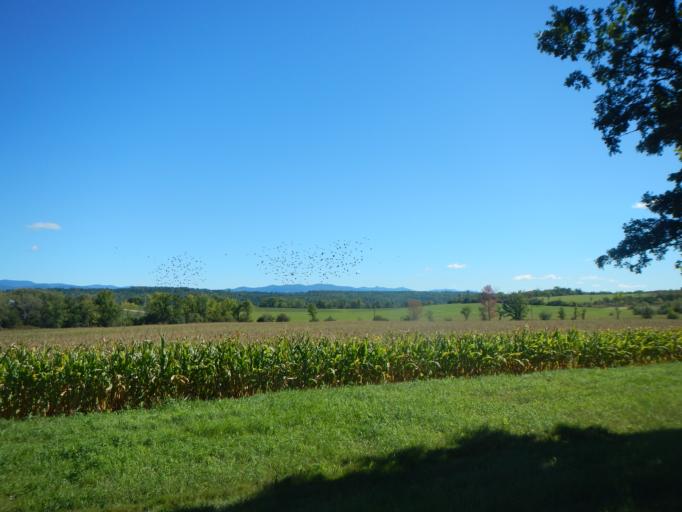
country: US
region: Vermont
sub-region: Addison County
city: Middlebury (village)
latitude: 44.0190
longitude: -73.2564
